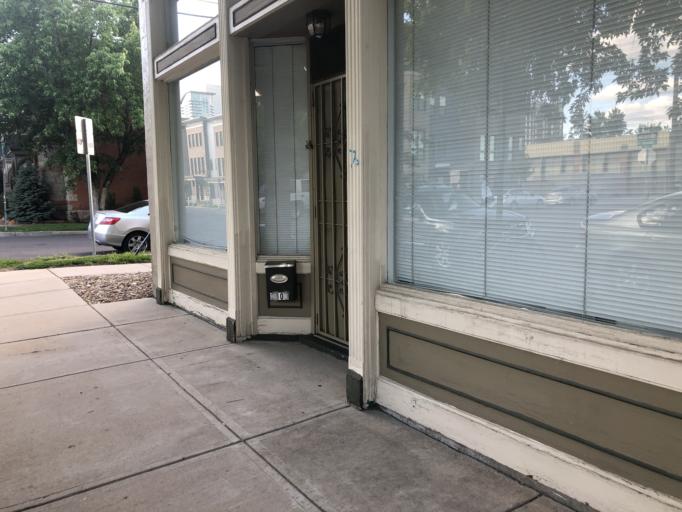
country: US
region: Colorado
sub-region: Denver County
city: Denver
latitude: 39.7536
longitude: -104.9834
